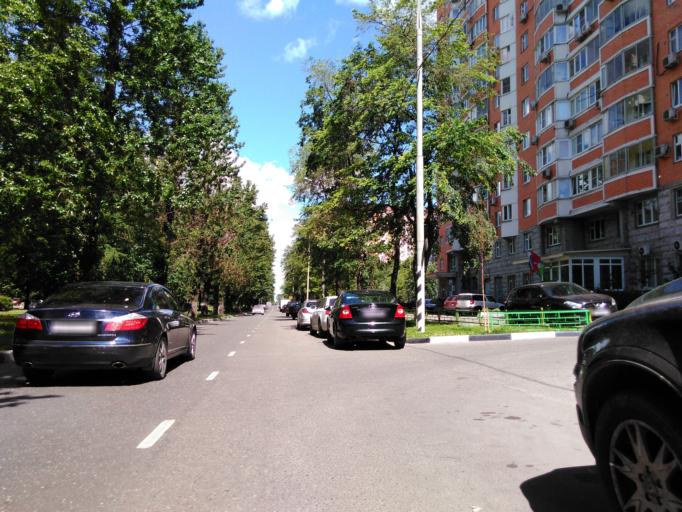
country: RU
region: Moskovskaya
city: Cheremushki
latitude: 55.6702
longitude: 37.5675
